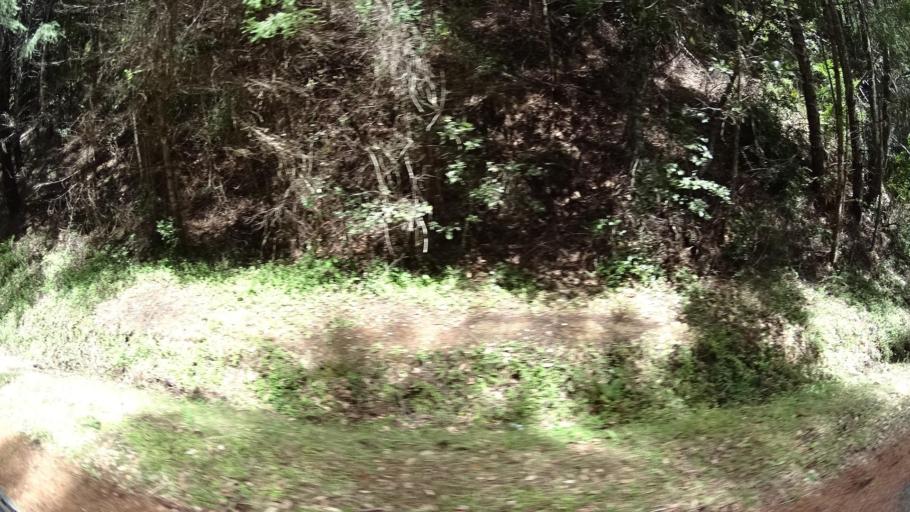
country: US
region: California
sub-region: Humboldt County
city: Blue Lake
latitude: 40.7592
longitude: -123.9214
